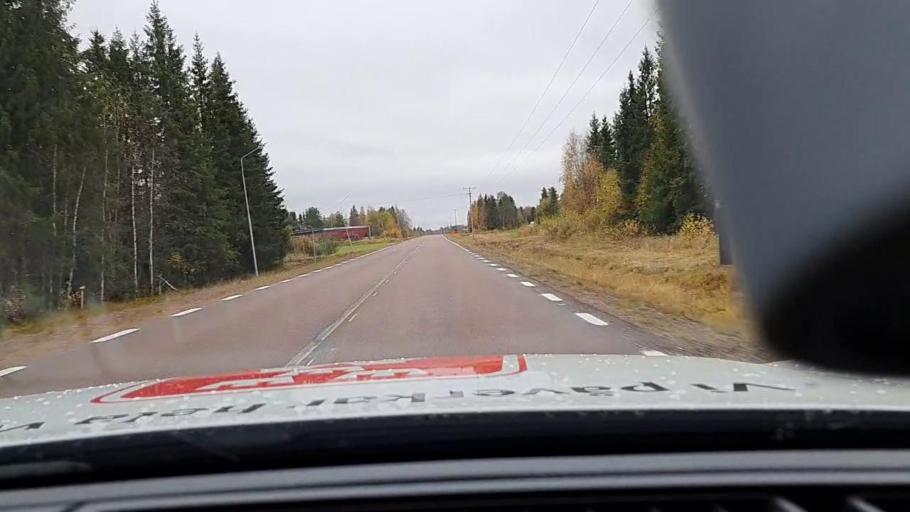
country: FI
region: Lapland
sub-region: Torniolaakso
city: Ylitornio
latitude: 66.1435
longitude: 23.8973
